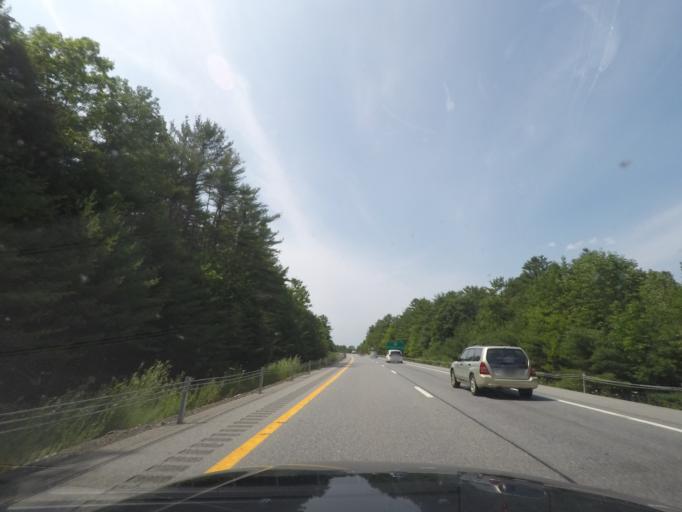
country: US
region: New York
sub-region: Warren County
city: Warrensburg
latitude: 43.6641
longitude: -73.7710
